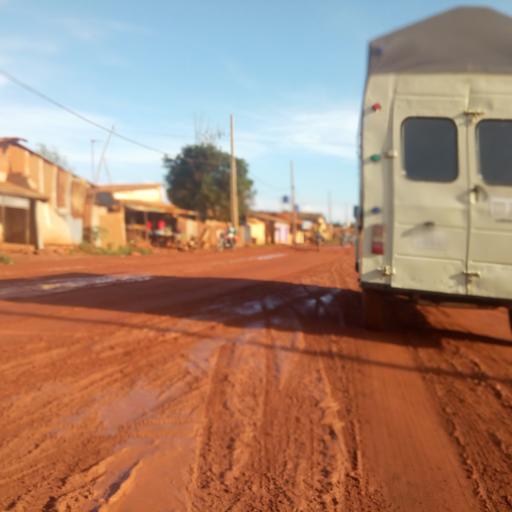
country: BJ
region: Atlantique
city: Hevie
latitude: 6.4139
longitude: 2.2642
